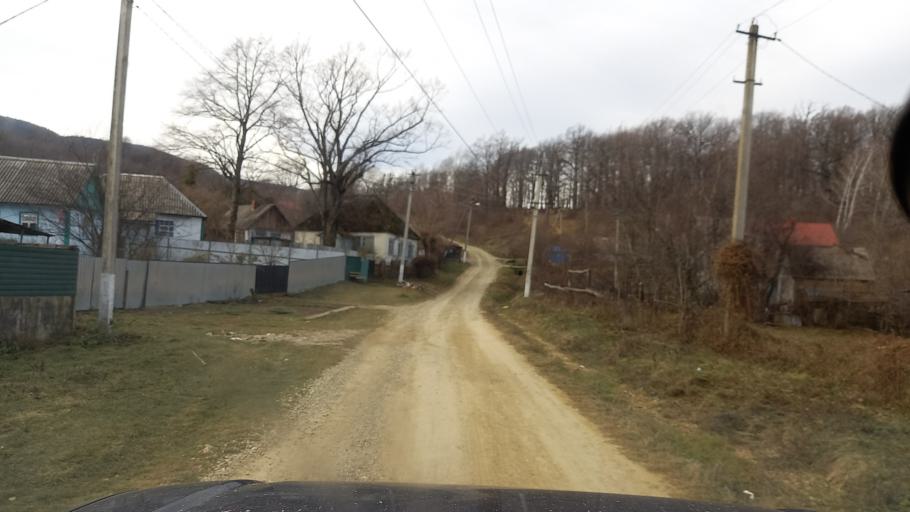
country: RU
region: Krasnodarskiy
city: Neftegorsk
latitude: 44.2297
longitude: 39.9014
